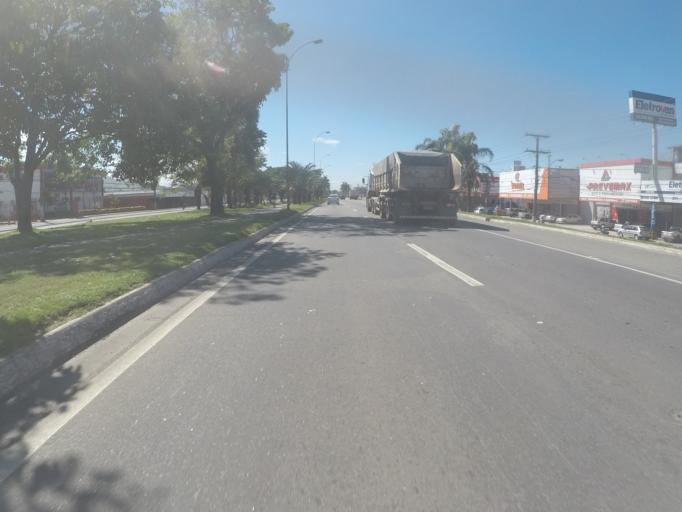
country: BR
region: Espirito Santo
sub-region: Serra
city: Serra
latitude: -20.2195
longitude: -40.2701
